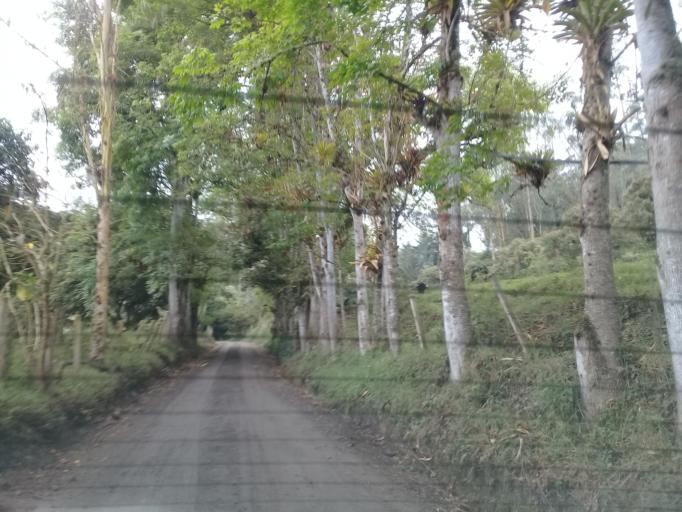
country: CO
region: Cundinamarca
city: Caqueza
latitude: 4.3922
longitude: -73.9799
